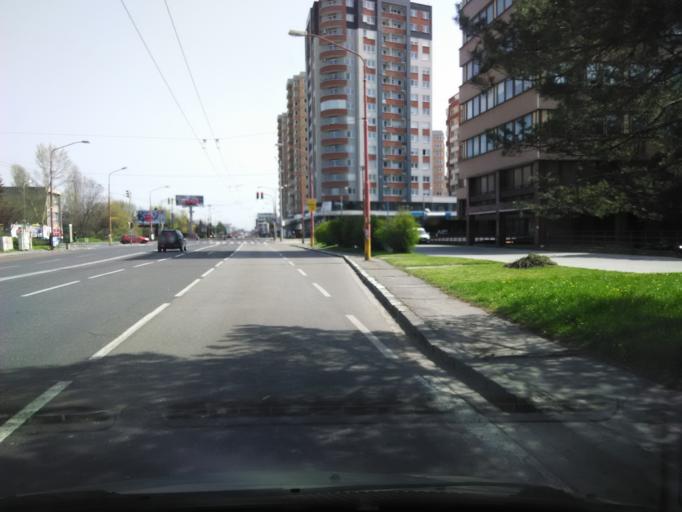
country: SK
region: Bratislavsky
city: Bratislava
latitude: 48.1500
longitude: 17.1646
